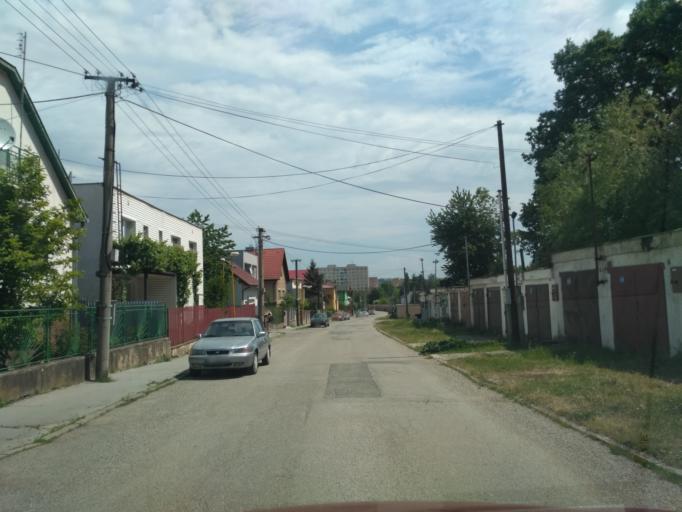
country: SK
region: Kosicky
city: Kosice
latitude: 48.7260
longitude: 21.2332
